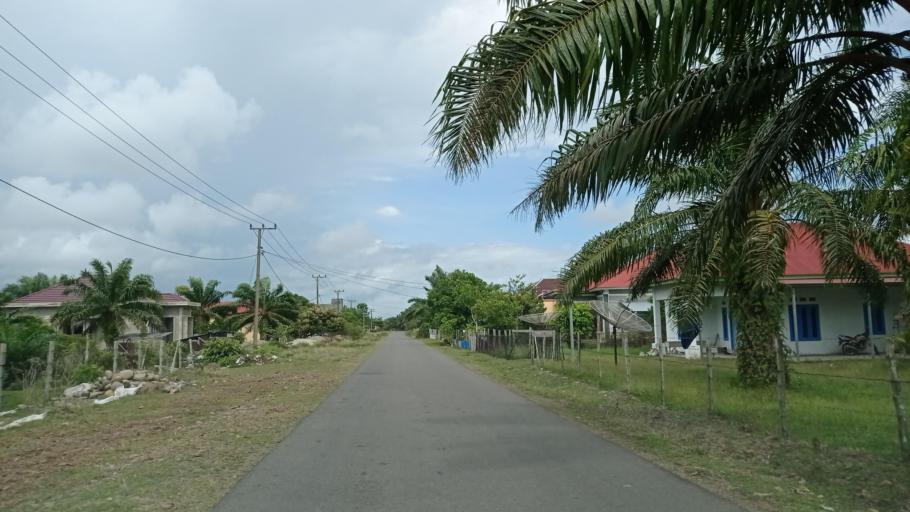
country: ID
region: Bengkulu
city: Ipuh
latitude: -2.5662
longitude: 101.1144
